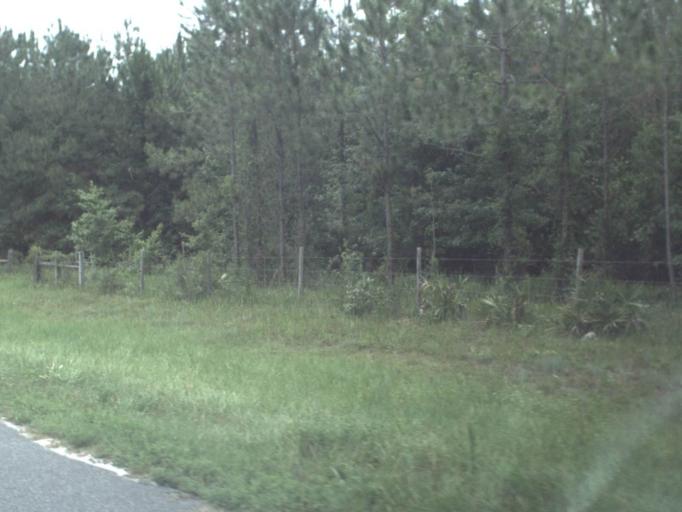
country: US
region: Florida
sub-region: Clay County
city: Middleburg
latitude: 29.9736
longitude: -81.8977
